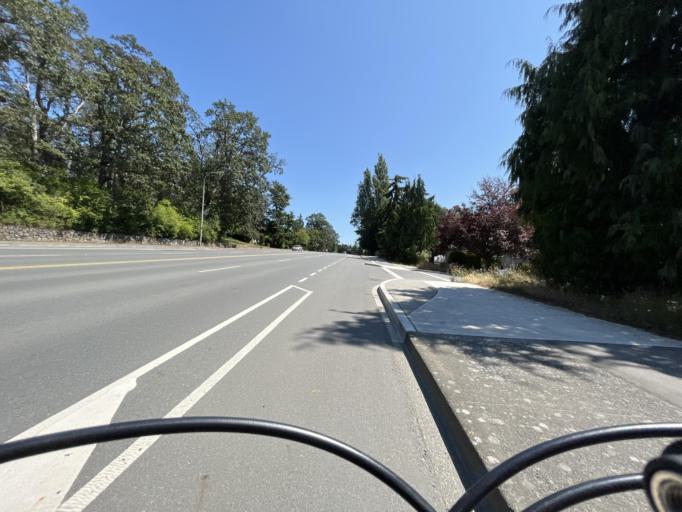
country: CA
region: British Columbia
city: Victoria
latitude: 48.4706
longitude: -123.3435
